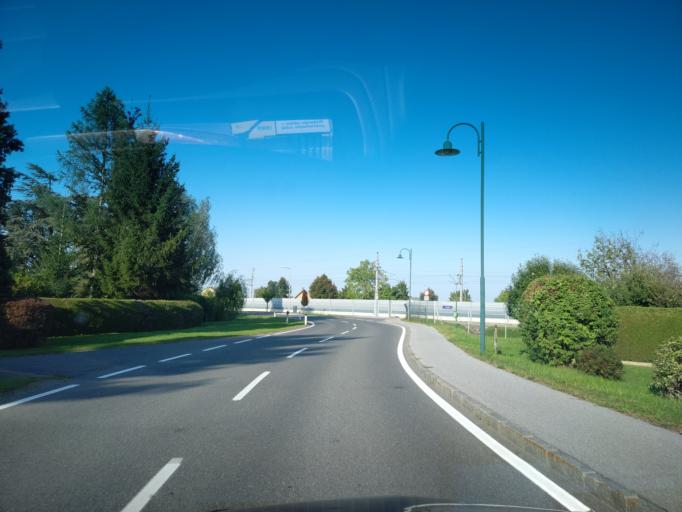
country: AT
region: Styria
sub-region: Politischer Bezirk Leibnitz
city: Kaindorf an der Sulm
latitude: 46.8030
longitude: 15.5414
